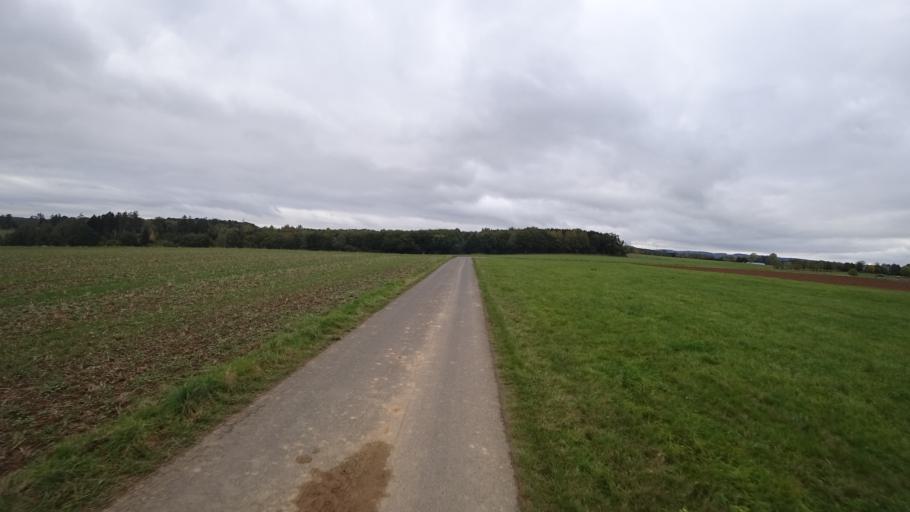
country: DE
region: Rheinland-Pfalz
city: Marienrachdorf
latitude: 50.5477
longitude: 7.6964
